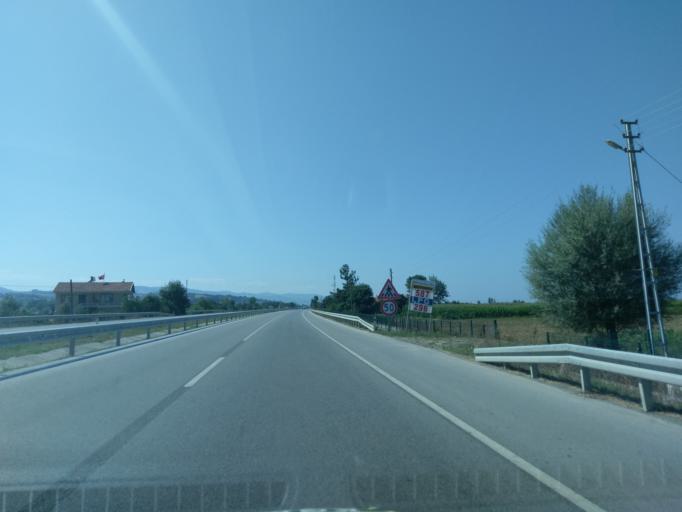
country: TR
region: Samsun
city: Alacam
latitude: 41.6086
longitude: 35.6653
